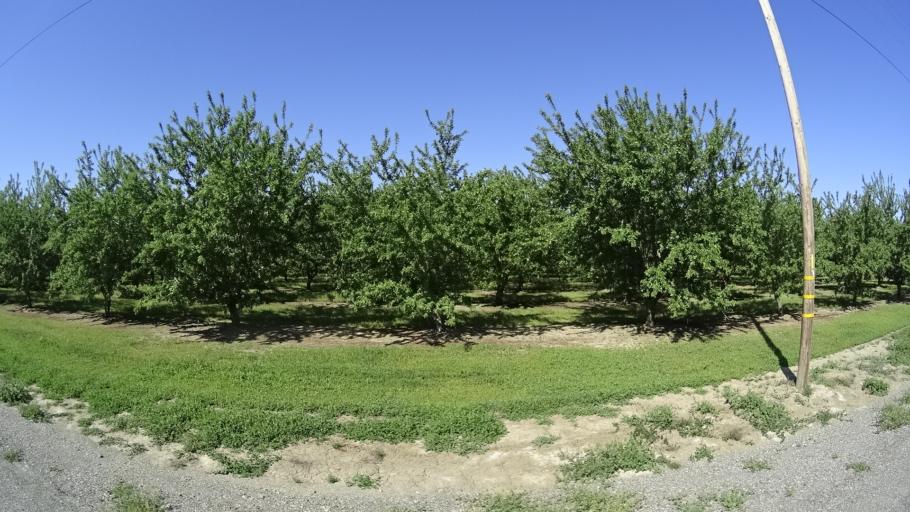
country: US
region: California
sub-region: Glenn County
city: Hamilton City
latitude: 39.7282
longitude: -122.0214
